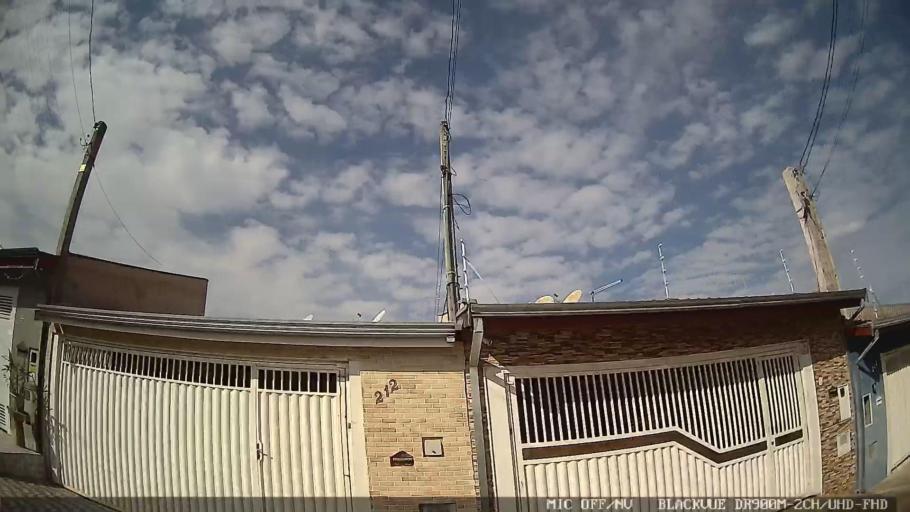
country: BR
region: Sao Paulo
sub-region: Salto
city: Salto
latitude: -23.1829
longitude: -47.2612
